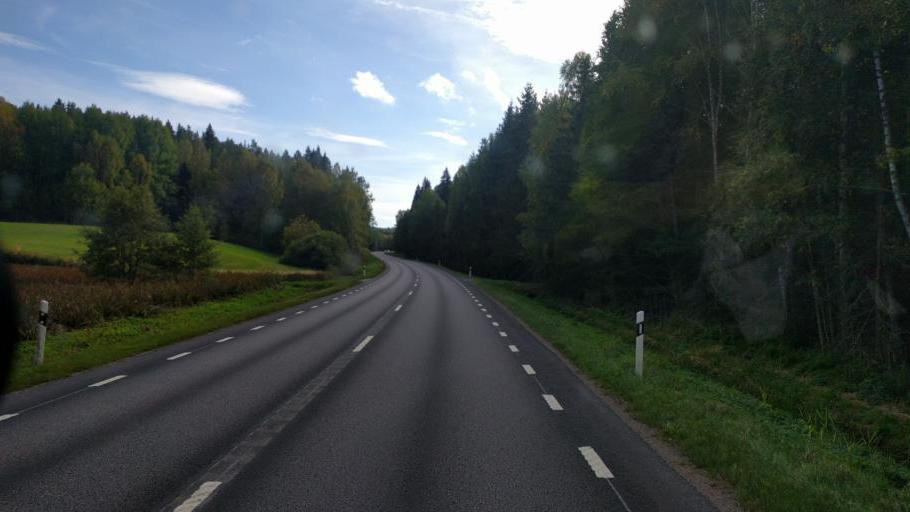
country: SE
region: OEstergoetland
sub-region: Kinda Kommun
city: Kisa
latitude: 57.9546
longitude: 15.6609
